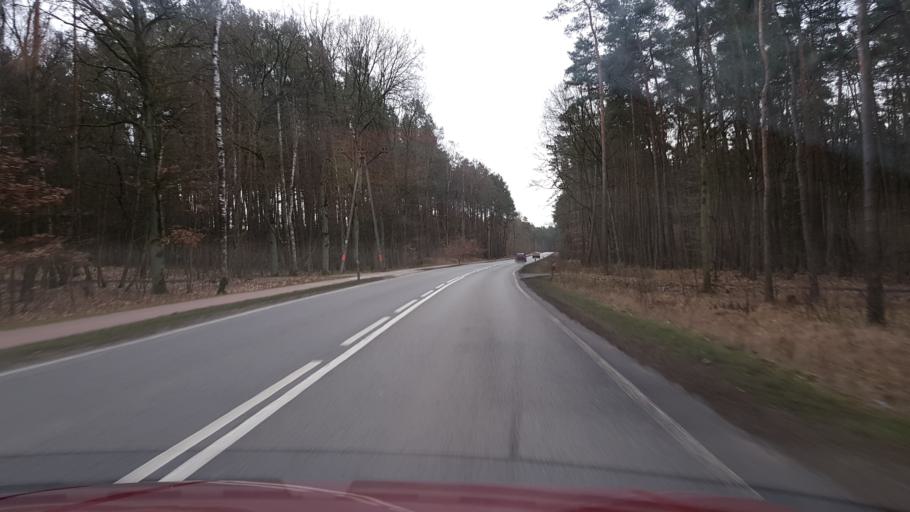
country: PL
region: West Pomeranian Voivodeship
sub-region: Powiat policki
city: Dobra
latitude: 53.5144
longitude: 14.4734
